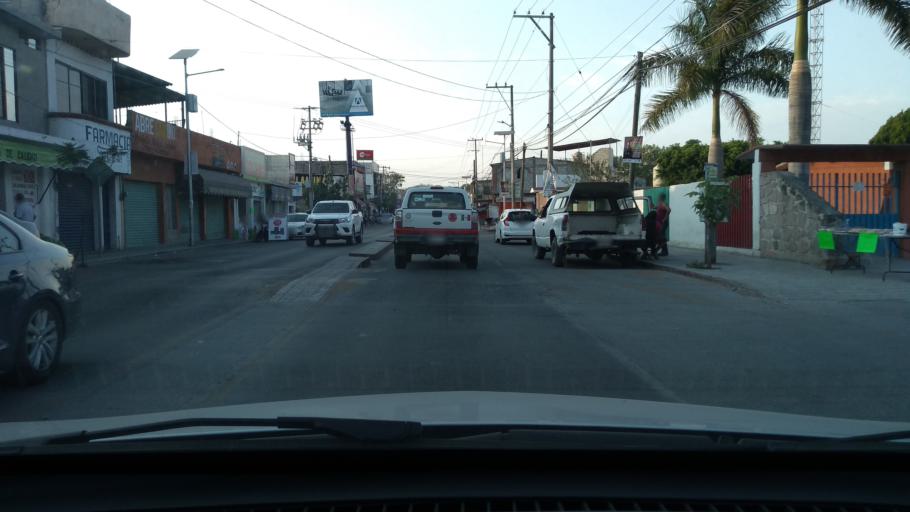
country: MX
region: Morelos
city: Puente de Ixtla
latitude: 18.6276
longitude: -99.3222
